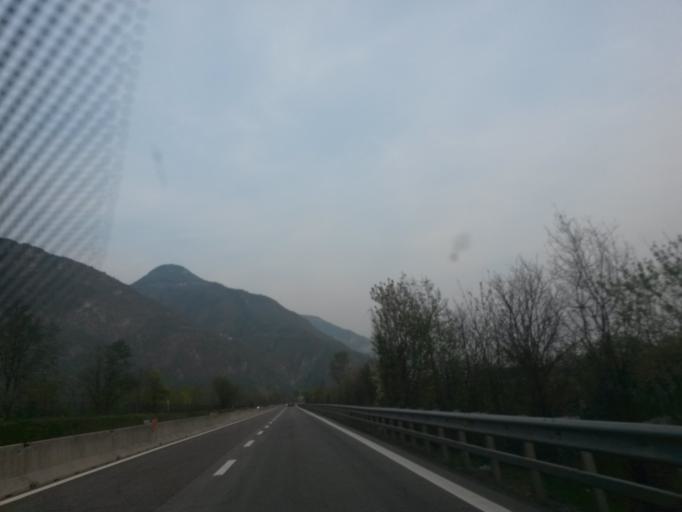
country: IT
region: Trentino-Alto Adige
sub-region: Bolzano
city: Gargazzone
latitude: 46.5694
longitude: 11.2064
